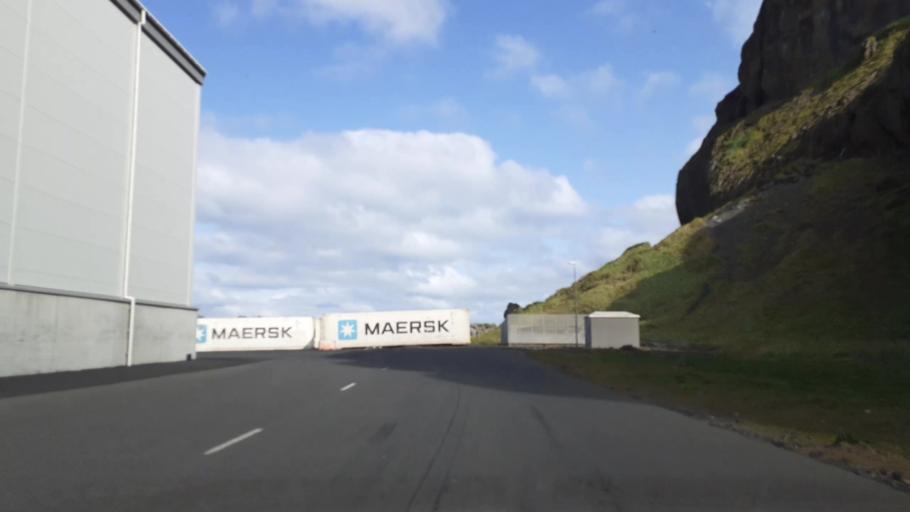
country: IS
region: South
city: Vestmannaeyjar
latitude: 63.4471
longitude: -20.2708
